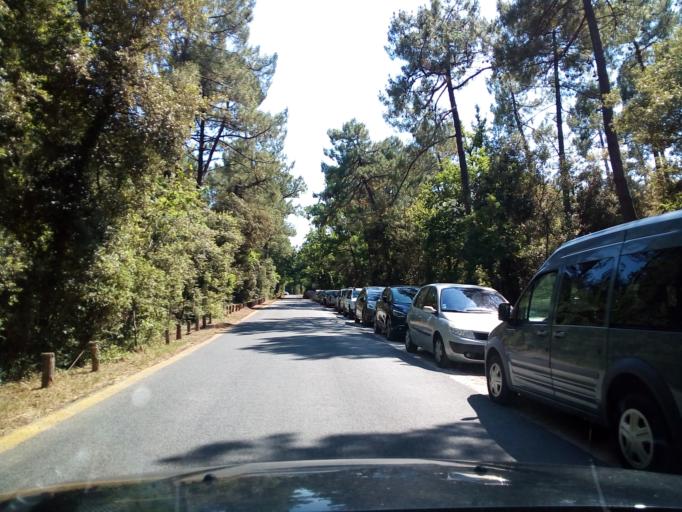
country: FR
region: Poitou-Charentes
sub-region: Departement de la Charente-Maritime
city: Boyard-Ville
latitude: 45.9842
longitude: -1.2944
